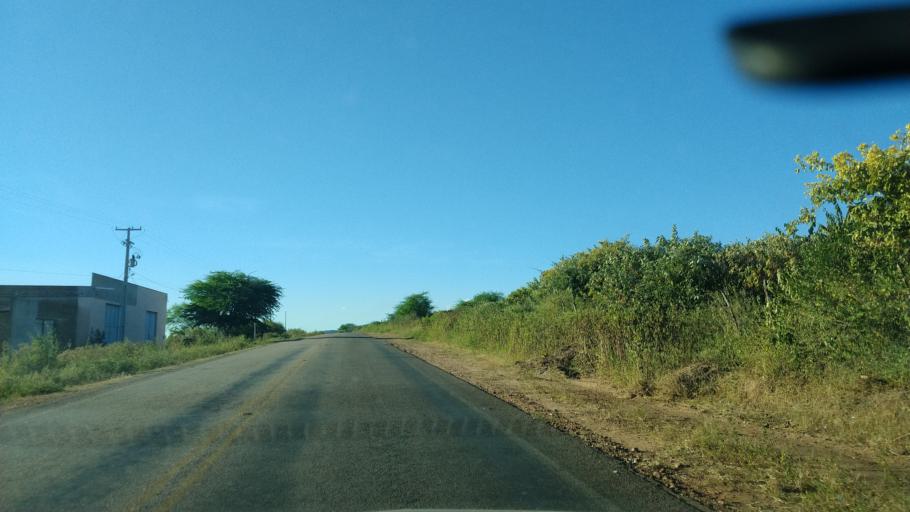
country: BR
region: Rio Grande do Norte
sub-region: Sao Jose Do Campestre
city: Sao Jose do Campestre
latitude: -6.3075
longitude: -35.7153
